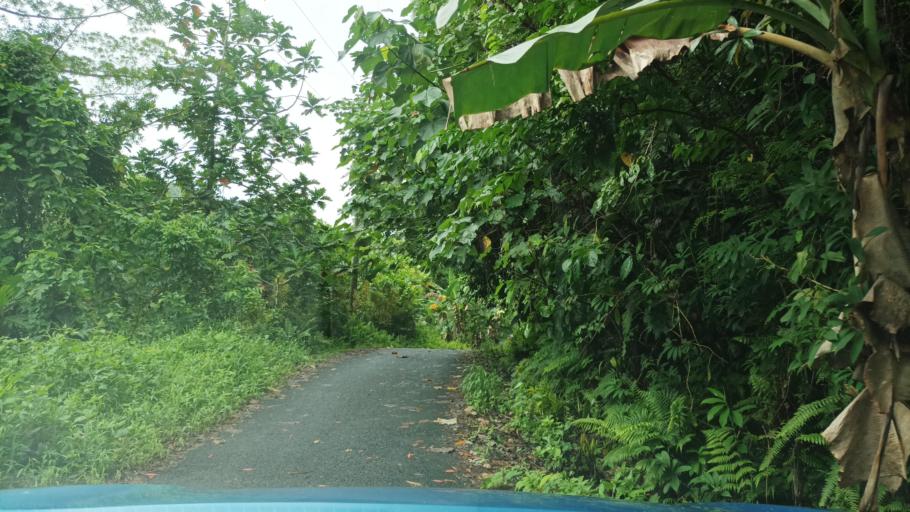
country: FM
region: Pohnpei
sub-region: Kolonia Municipality
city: Kolonia
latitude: 6.9191
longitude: 158.2758
